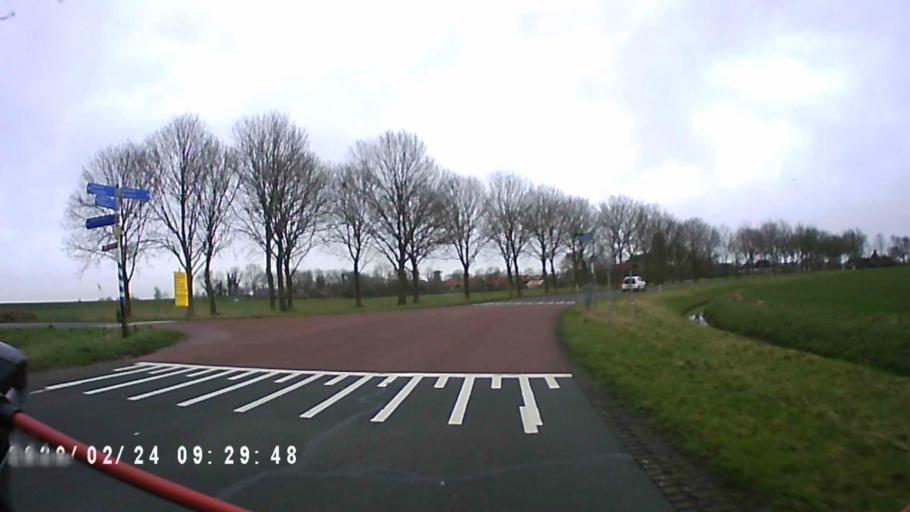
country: NL
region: Groningen
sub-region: Gemeente Winsum
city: Winsum
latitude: 53.3073
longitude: 6.4874
